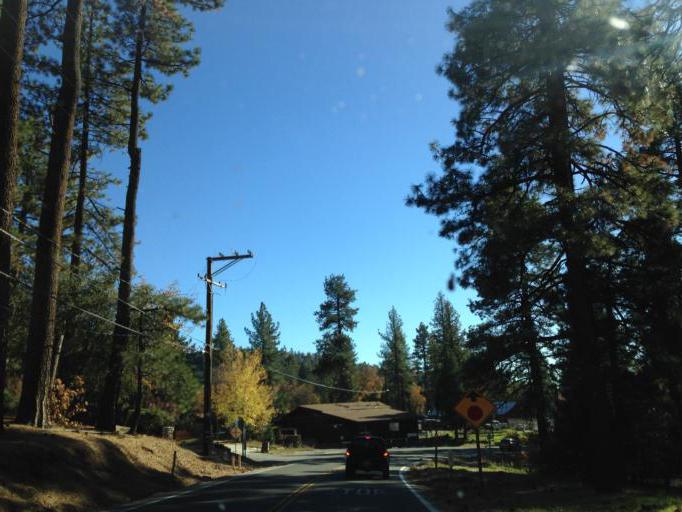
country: US
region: California
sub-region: Riverside County
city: Idyllwild
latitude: 33.7485
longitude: -116.7140
